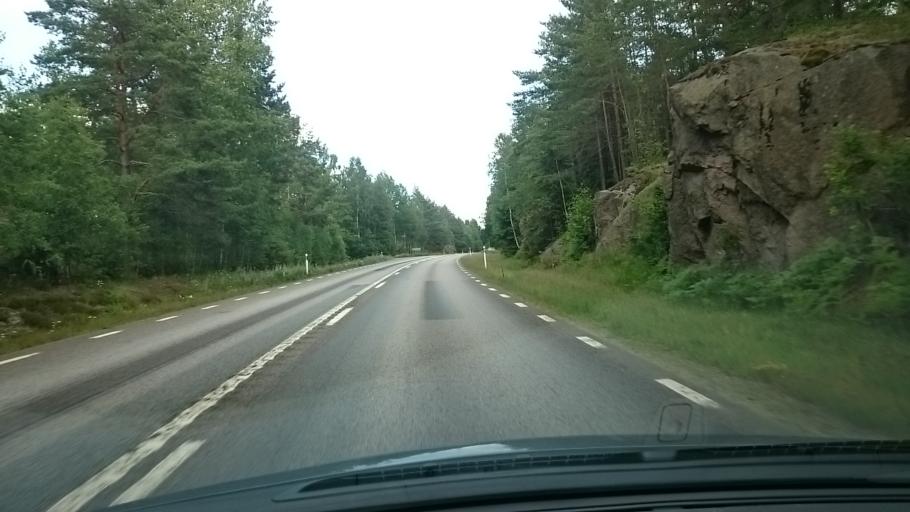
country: SE
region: OErebro
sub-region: Askersunds Kommun
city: Askersund
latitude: 58.7092
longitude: 14.7205
